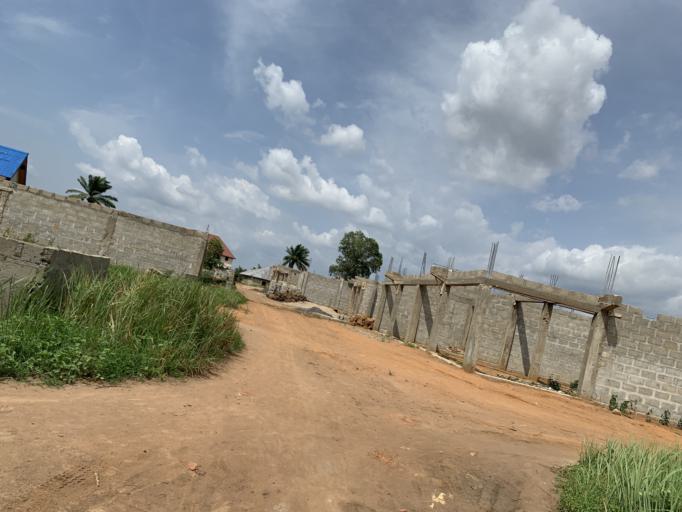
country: SL
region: Western Area
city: Waterloo
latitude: 8.3533
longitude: -13.0442
